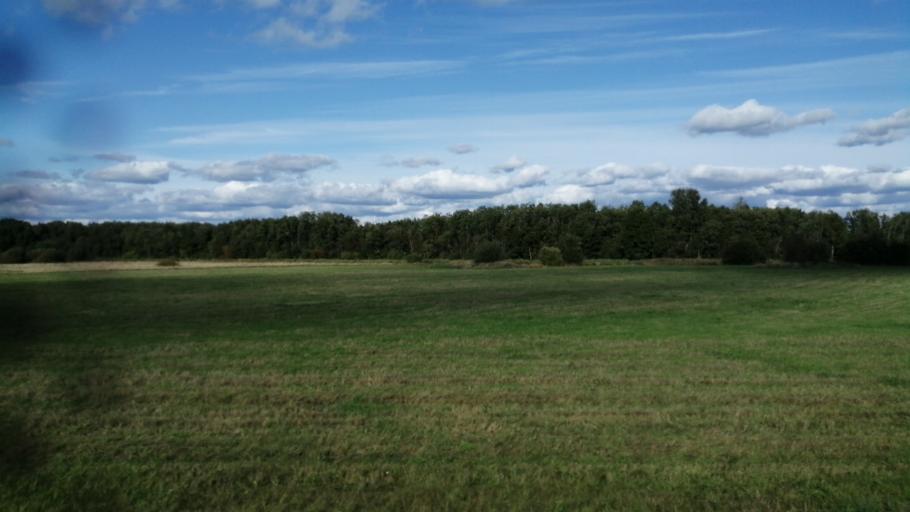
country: EE
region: Jogevamaa
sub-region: Poltsamaa linn
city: Poltsamaa
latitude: 58.6710
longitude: 25.9360
